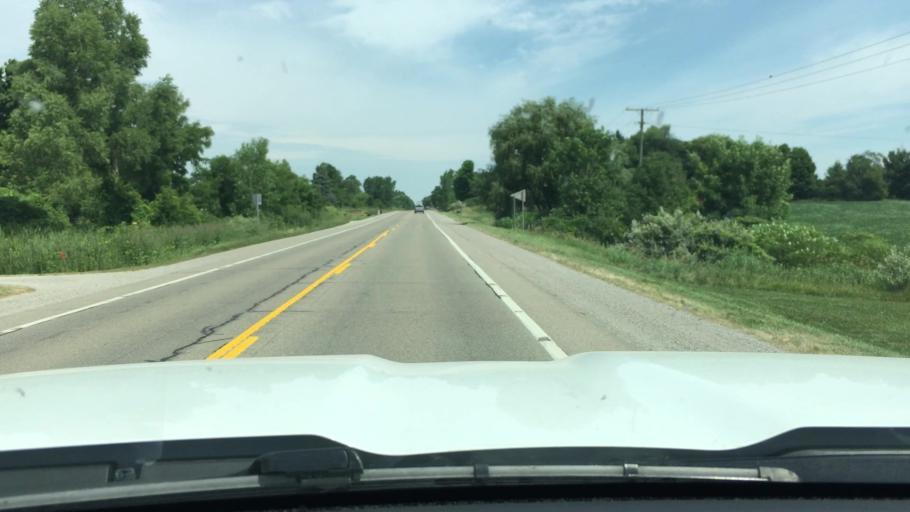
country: US
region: Michigan
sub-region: Lapeer County
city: Imlay City
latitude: 43.1181
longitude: -83.0728
